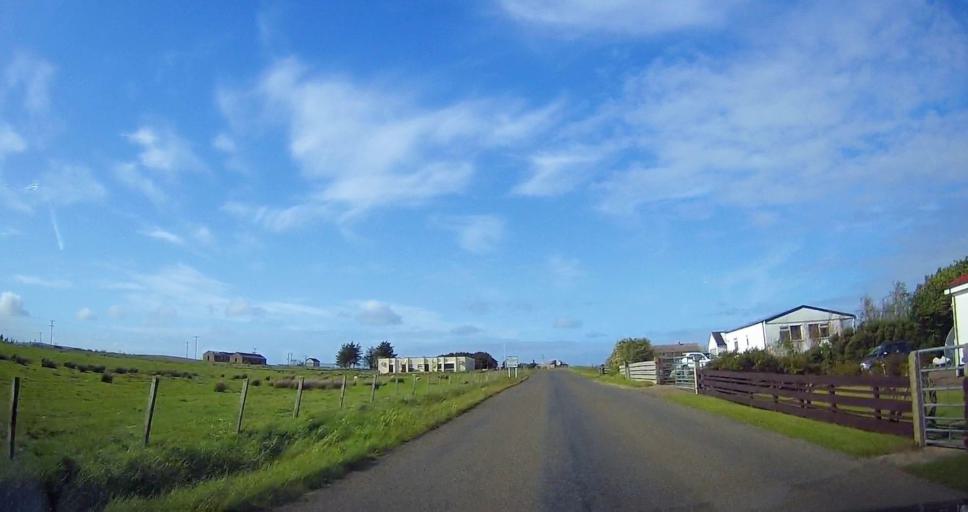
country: GB
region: Scotland
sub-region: Orkney Islands
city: Stromness
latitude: 58.8299
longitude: -3.2075
